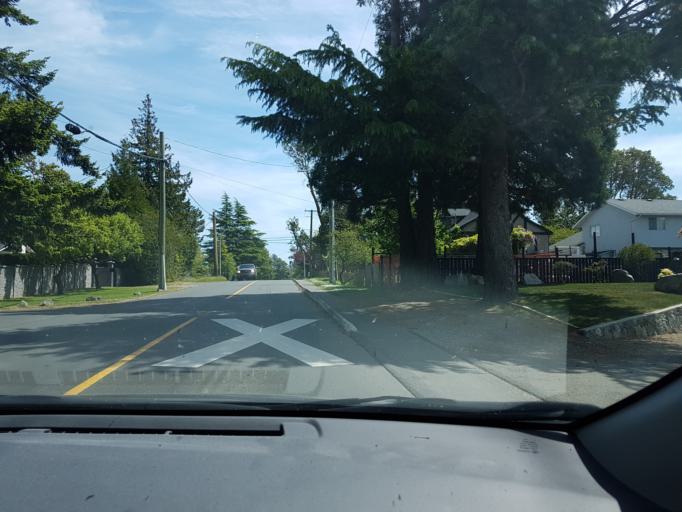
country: CA
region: British Columbia
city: Oak Bay
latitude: 48.4910
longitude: -123.3231
